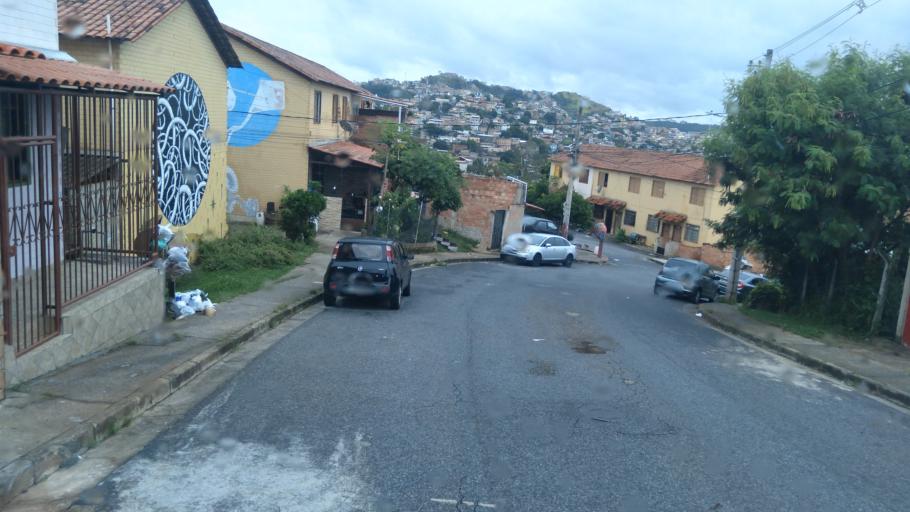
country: BR
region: Minas Gerais
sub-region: Belo Horizonte
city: Belo Horizonte
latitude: -19.9075
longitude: -43.8860
